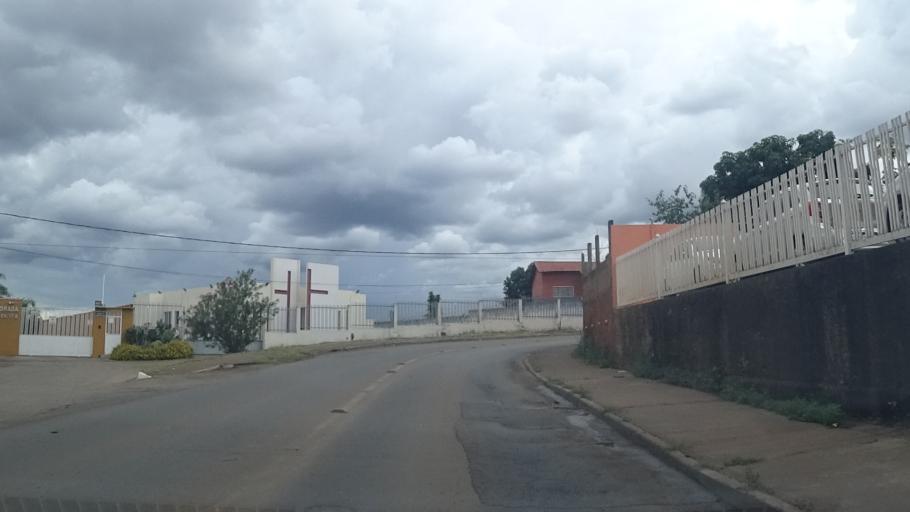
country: BR
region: Federal District
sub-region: Brasilia
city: Brasilia
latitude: -15.8479
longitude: -48.0261
